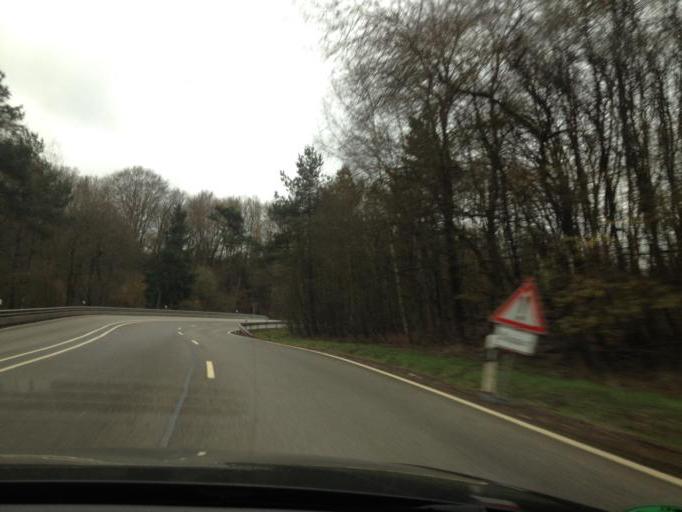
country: DE
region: Rheinland-Pfalz
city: Oberbrombach
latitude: 49.7052
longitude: 7.2605
